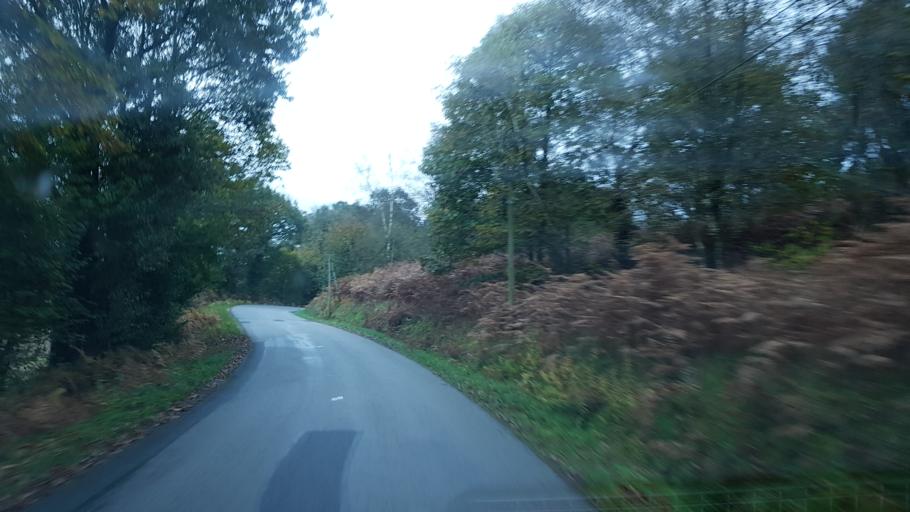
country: FR
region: Brittany
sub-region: Departement du Morbihan
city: Sulniac
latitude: 47.6941
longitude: -2.5800
